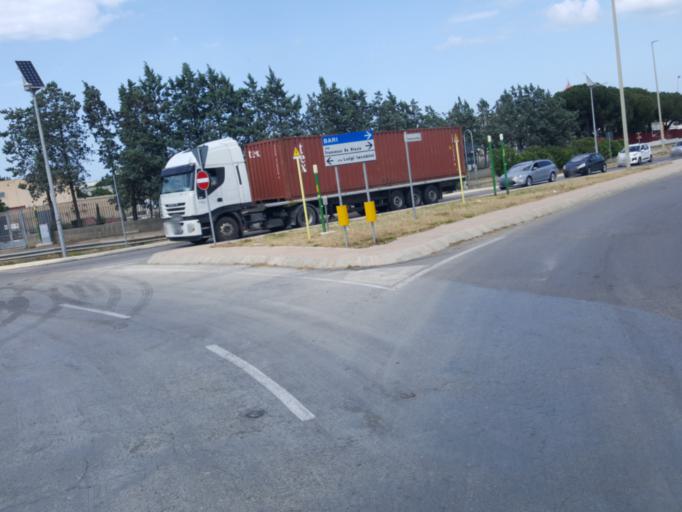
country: IT
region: Apulia
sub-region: Provincia di Bari
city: San Paolo
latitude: 41.1143
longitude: 16.8050
